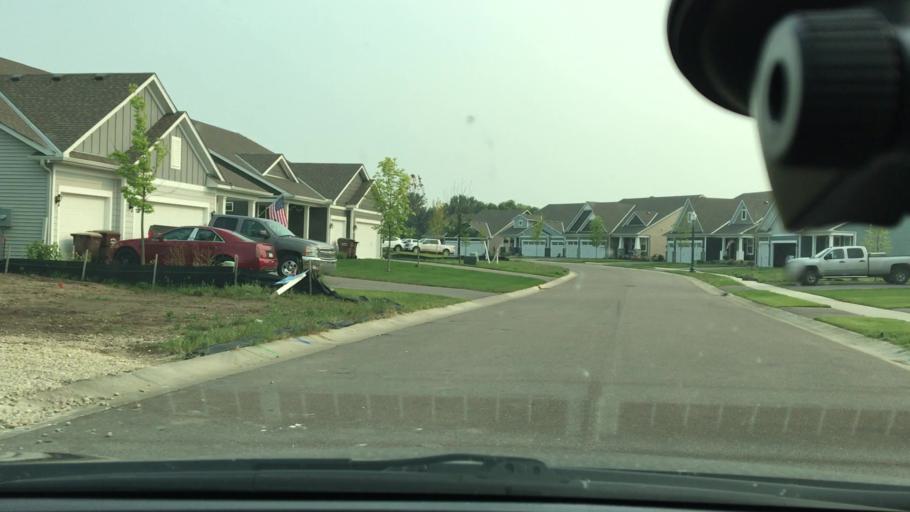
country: US
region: Minnesota
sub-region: Hennepin County
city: Champlin
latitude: 45.1982
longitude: -93.4365
